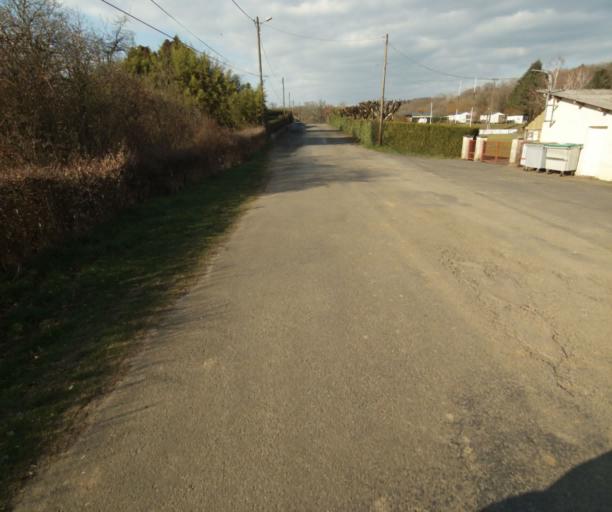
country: FR
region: Limousin
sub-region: Departement de la Correze
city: Saint-Clement
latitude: 45.3486
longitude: 1.6448
